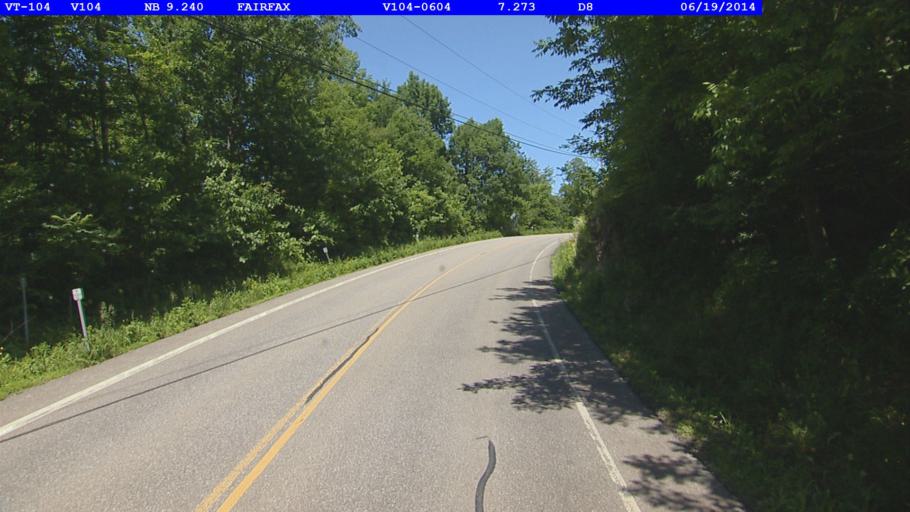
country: US
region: Vermont
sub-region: Chittenden County
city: Milton
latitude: 44.6899
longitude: -73.0331
